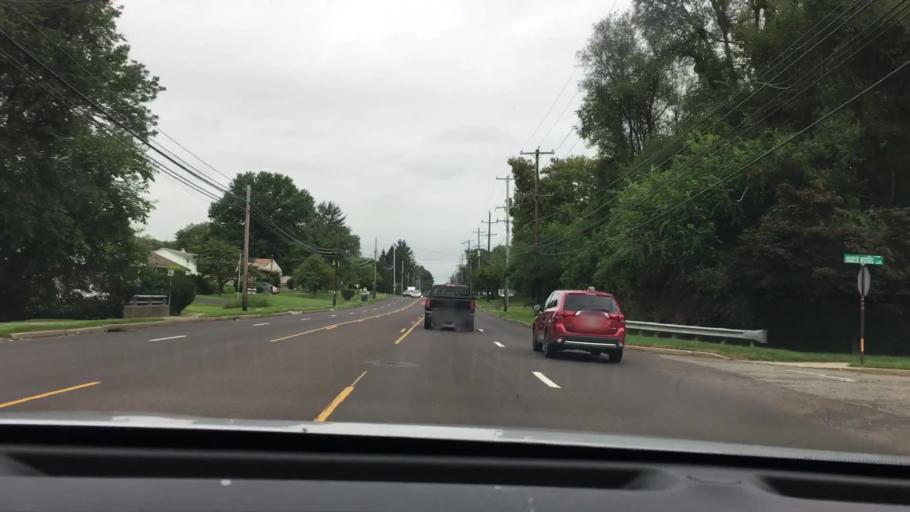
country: US
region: Pennsylvania
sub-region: Montgomery County
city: Hatboro
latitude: 40.1947
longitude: -75.1110
